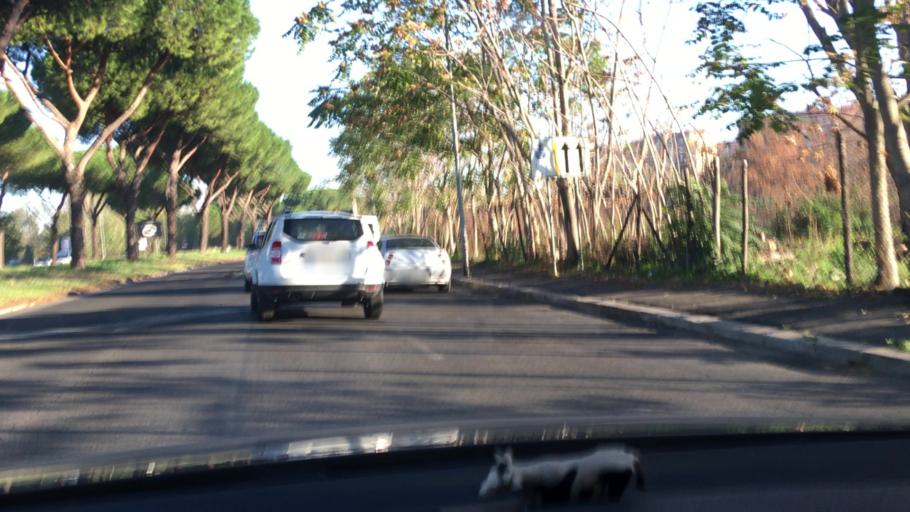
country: IT
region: Latium
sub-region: Citta metropolitana di Roma Capitale
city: Rome
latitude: 41.8660
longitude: 12.5679
